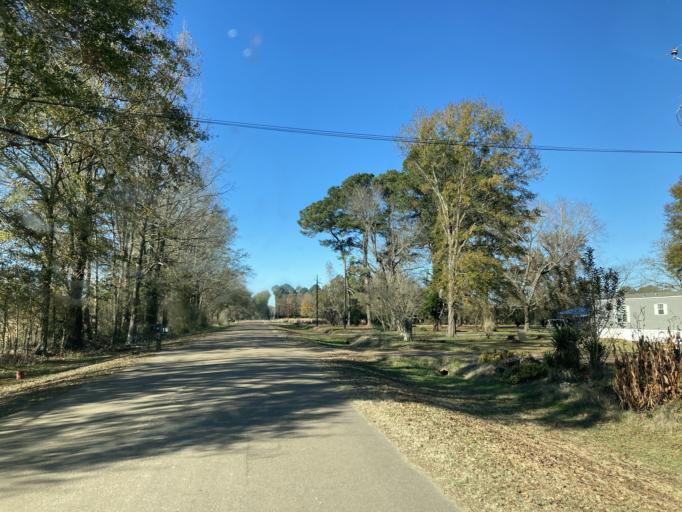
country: US
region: Mississippi
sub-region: Madison County
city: Kearney Park
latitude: 32.6040
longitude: -90.4017
